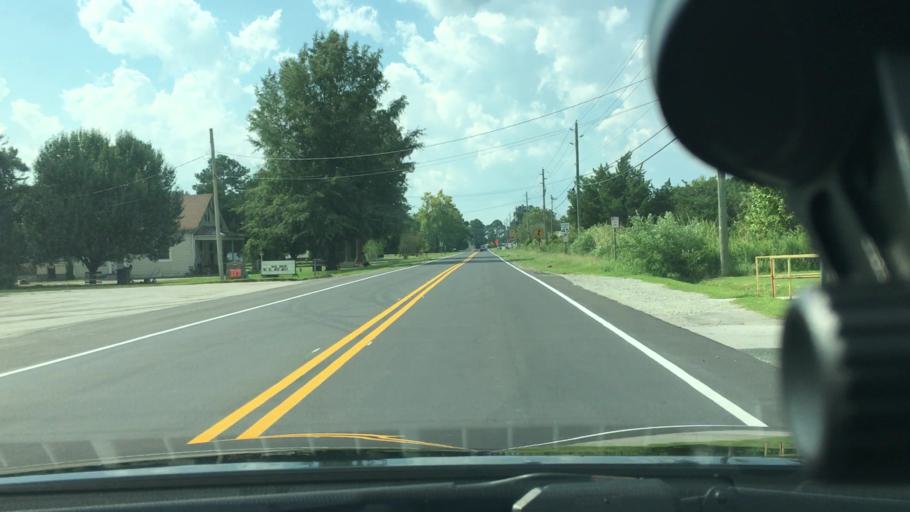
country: US
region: North Carolina
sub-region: Craven County
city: James City
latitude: 35.0731
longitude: -77.0237
